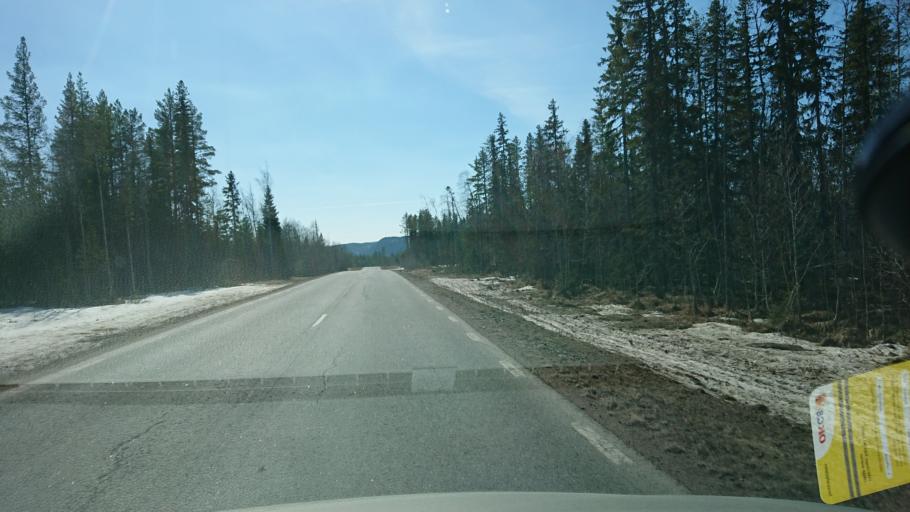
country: SE
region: Vaesternorrland
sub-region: Solleftea Kommun
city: As
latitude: 63.5848
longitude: 16.4360
